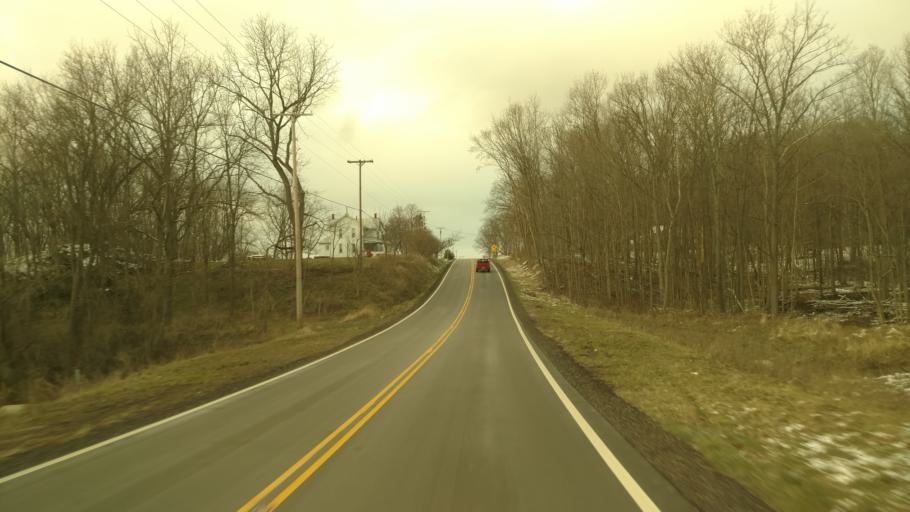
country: US
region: Ohio
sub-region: Ashland County
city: Ashland
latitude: 40.8388
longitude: -82.2129
